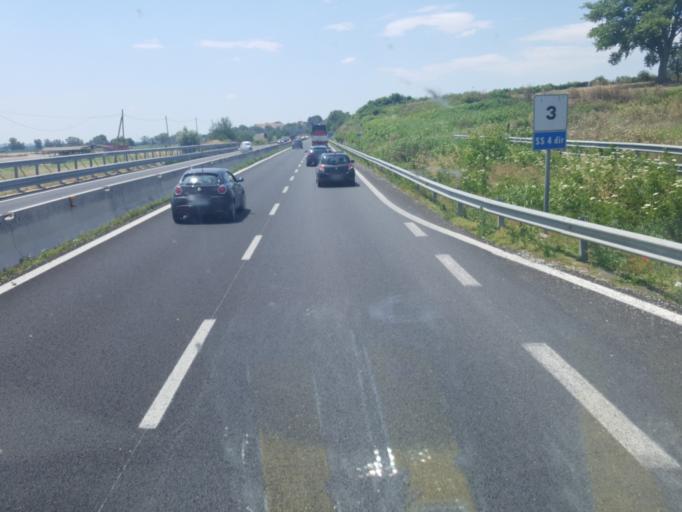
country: IT
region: Latium
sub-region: Citta metropolitana di Roma Capitale
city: Fiano Romano
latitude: 42.1473
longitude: 12.6192
